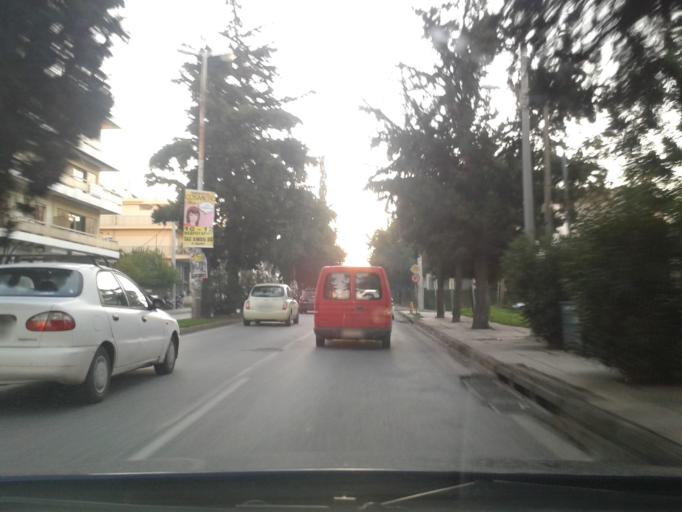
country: GR
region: Attica
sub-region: Nomarchia Athinas
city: Filothei
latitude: 38.0322
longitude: 23.7754
